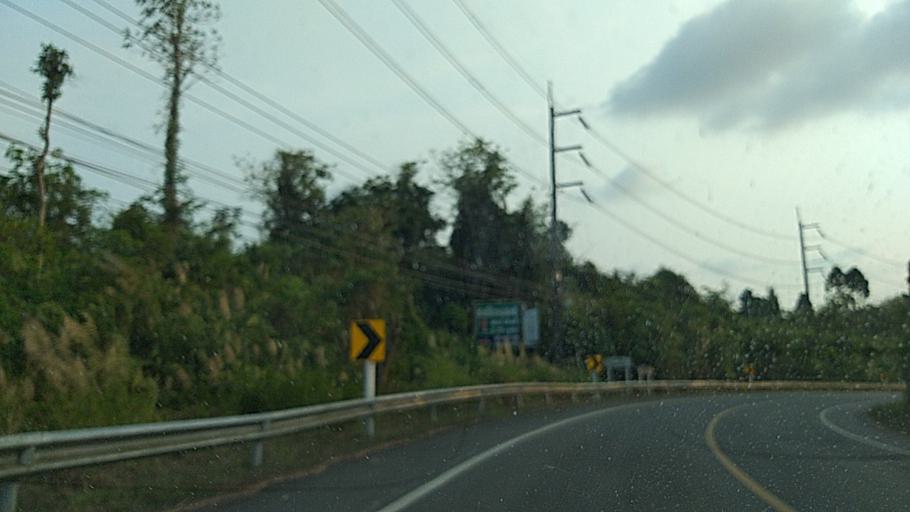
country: TH
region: Trat
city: Laem Ngop
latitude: 12.2662
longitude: 102.3054
